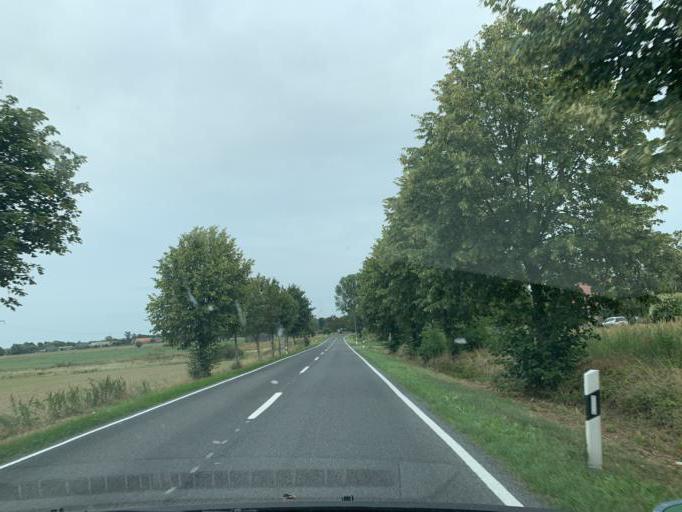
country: DE
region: Brandenburg
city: Gransee
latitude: 52.9984
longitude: 13.2388
